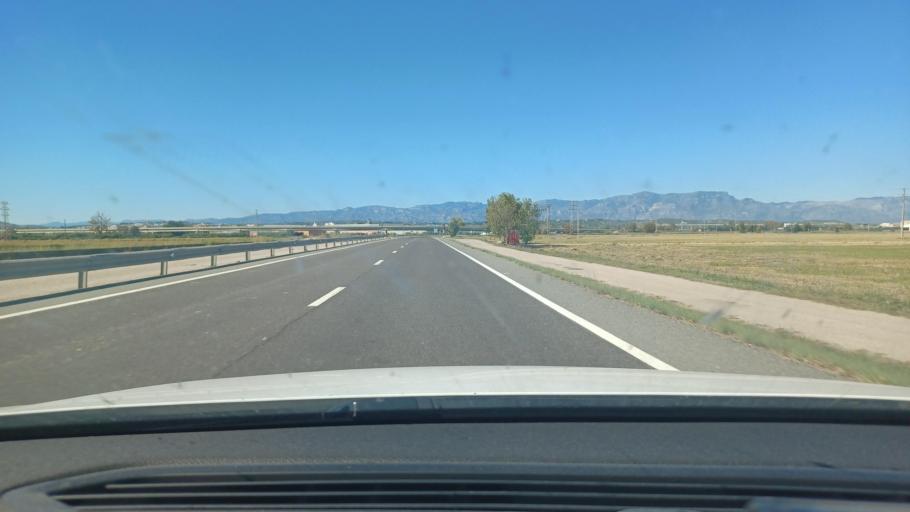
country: ES
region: Catalonia
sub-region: Provincia de Tarragona
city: Amposta
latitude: 40.7129
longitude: 0.6018
